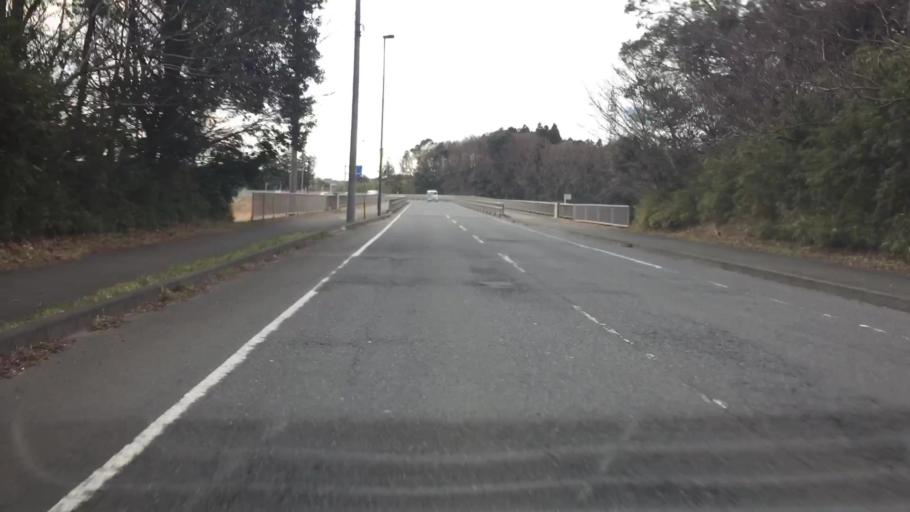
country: JP
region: Ibaraki
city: Ryugasaki
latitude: 35.8142
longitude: 140.1712
